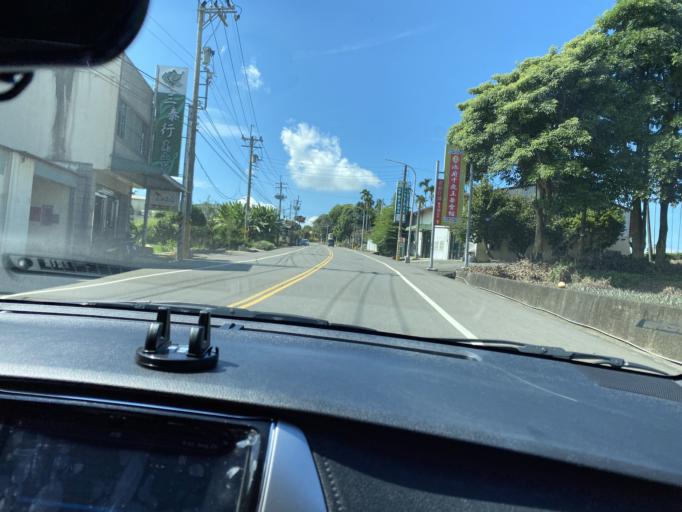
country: TW
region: Taiwan
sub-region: Nantou
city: Nantou
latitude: 23.8503
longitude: 120.6290
